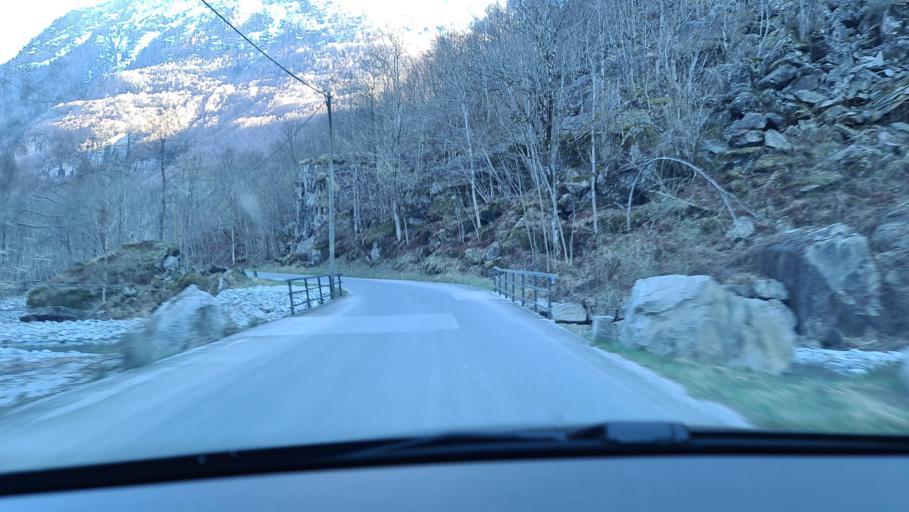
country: CH
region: Ticino
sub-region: Vallemaggia District
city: Cevio
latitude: 46.3825
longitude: 8.5415
